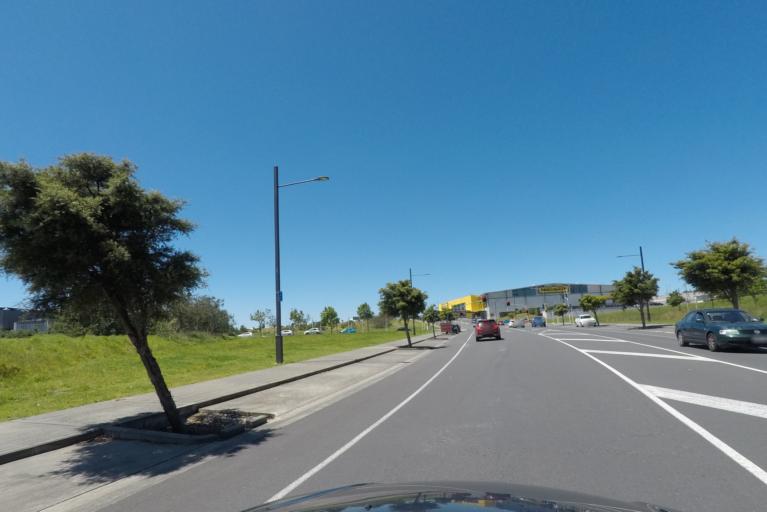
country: NZ
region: Auckland
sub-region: Auckland
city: Rosebank
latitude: -36.8183
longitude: 174.6081
